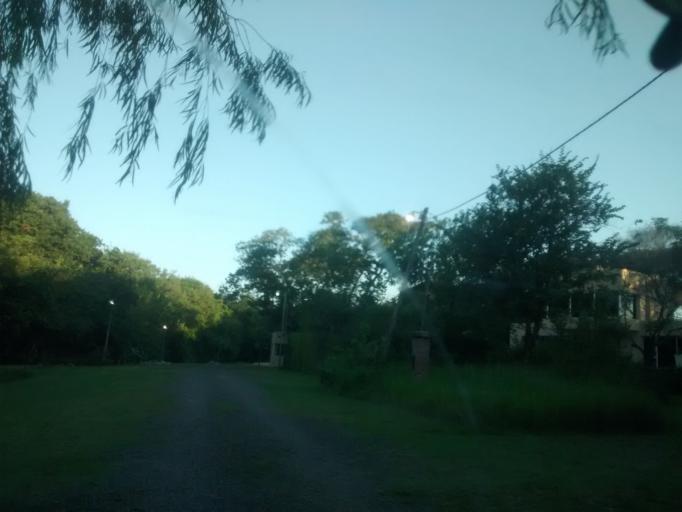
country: AR
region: Chaco
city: Fontana
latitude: -27.4186
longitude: -59.0090
